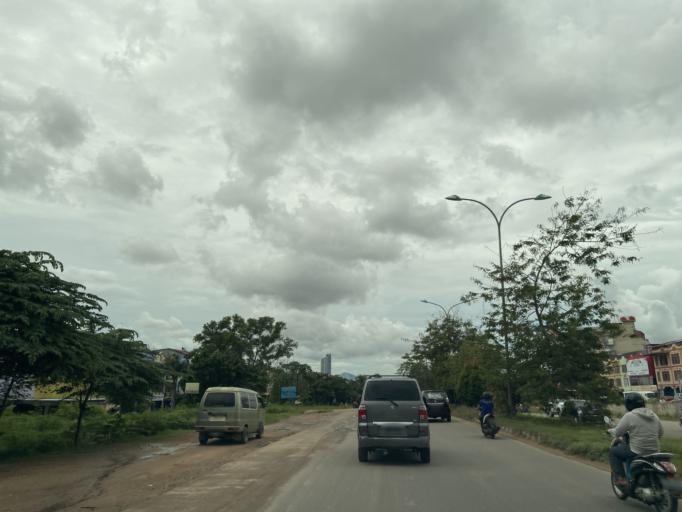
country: SG
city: Singapore
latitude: 1.1353
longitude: 104.0278
